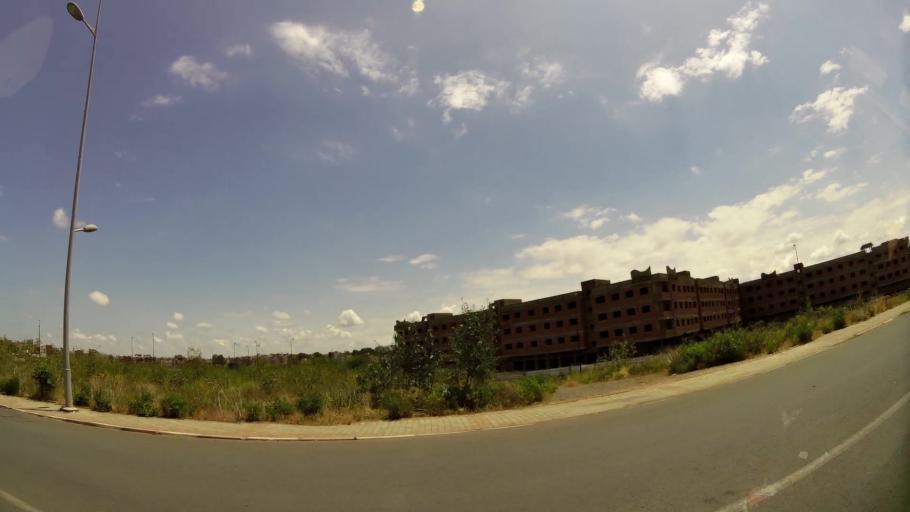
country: MA
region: Gharb-Chrarda-Beni Hssen
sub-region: Kenitra Province
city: Kenitra
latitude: 34.2577
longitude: -6.6114
